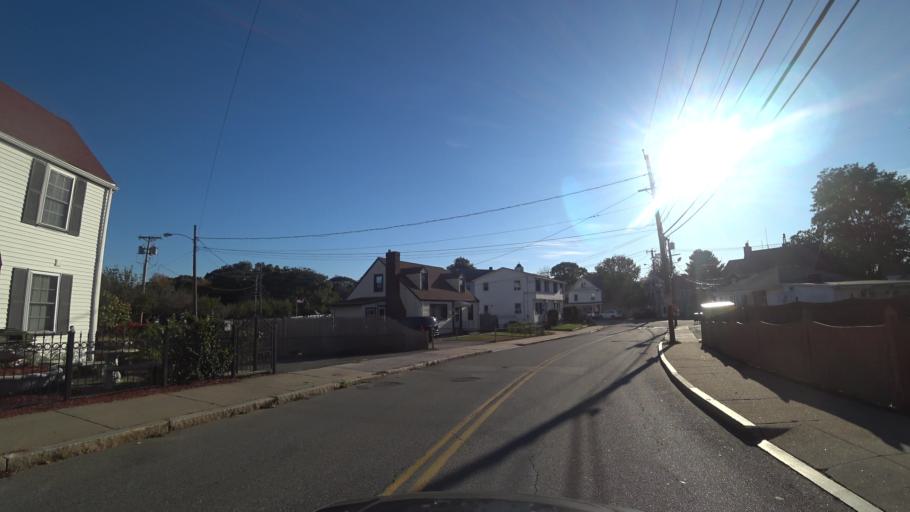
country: US
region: Massachusetts
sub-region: Middlesex County
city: Medford
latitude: 42.4360
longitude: -71.0956
